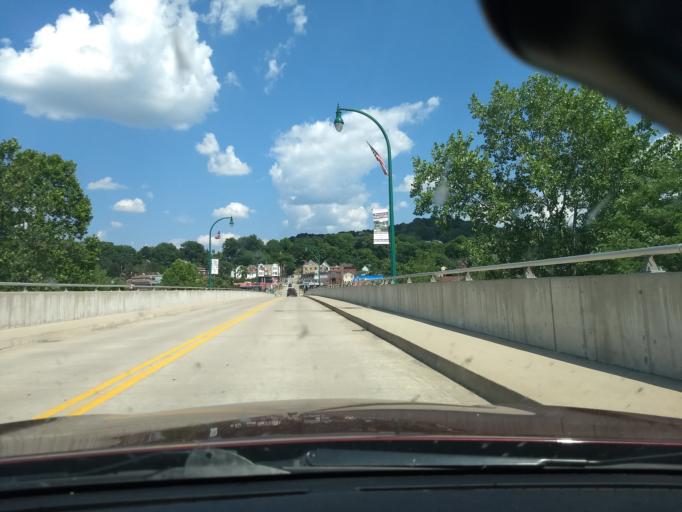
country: US
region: Pennsylvania
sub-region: Westmoreland County
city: Trafford
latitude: 40.3864
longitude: -79.7636
